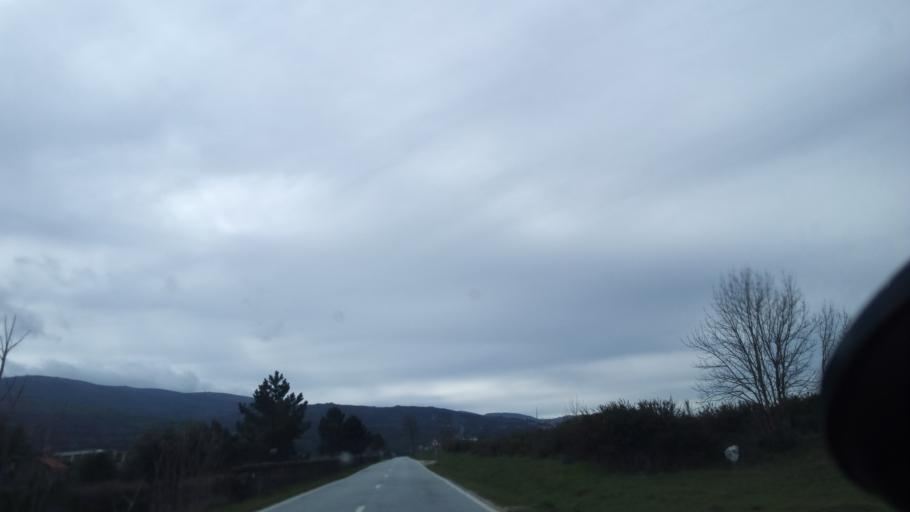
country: PT
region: Guarda
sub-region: Fornos de Algodres
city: Fornos de Algodres
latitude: 40.5405
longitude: -7.5696
